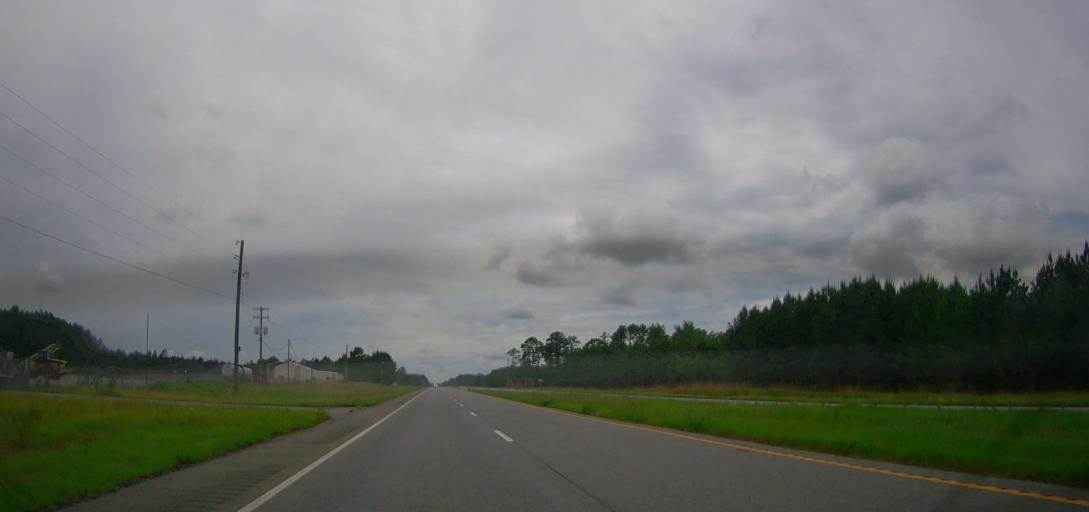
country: US
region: Georgia
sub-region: Appling County
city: Baxley
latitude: 31.7367
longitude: -82.2291
